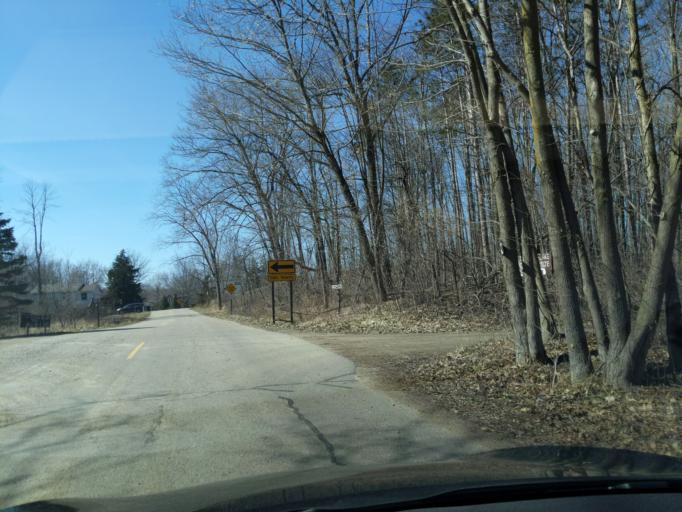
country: US
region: Michigan
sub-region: Ionia County
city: Lake Odessa
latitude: 42.7270
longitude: -85.0536
